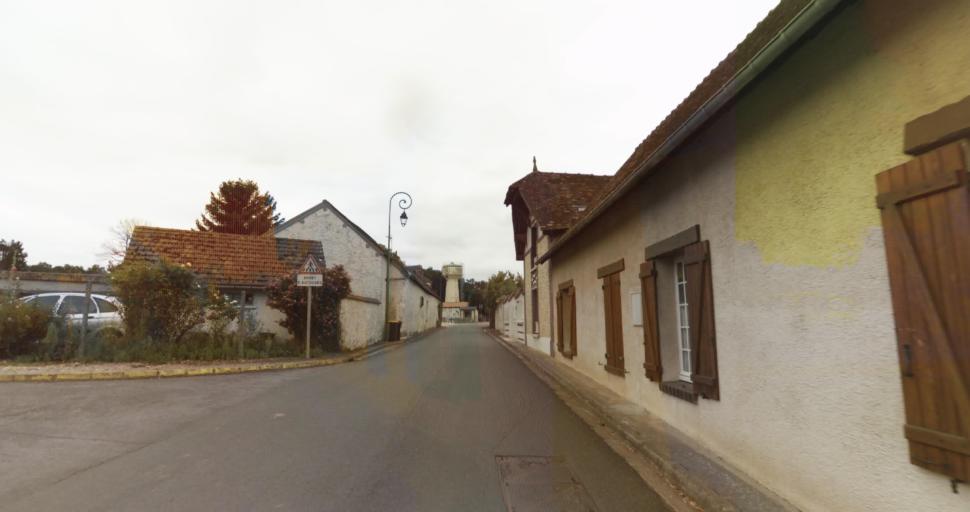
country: FR
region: Haute-Normandie
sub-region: Departement de l'Eure
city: Croth
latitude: 48.8719
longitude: 1.3580
